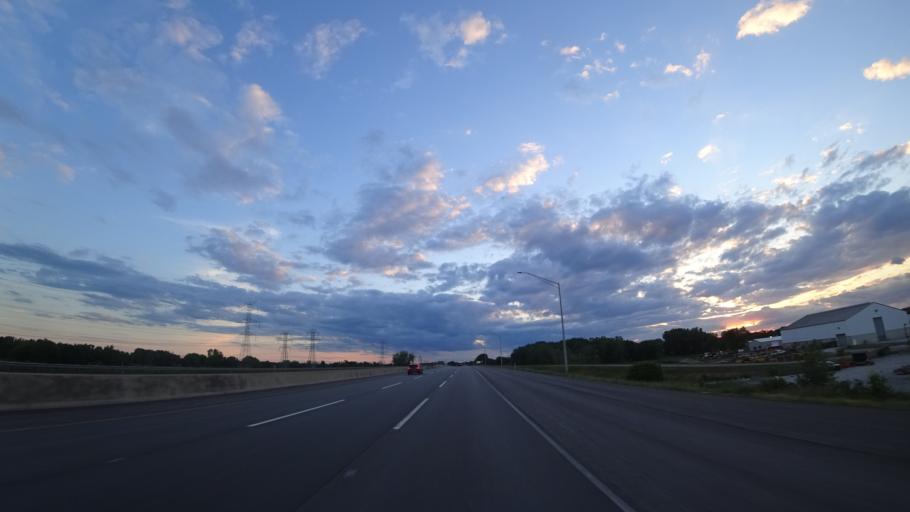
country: US
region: Indiana
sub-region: Lake County
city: Lake Station
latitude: 41.5927
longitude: -87.2444
